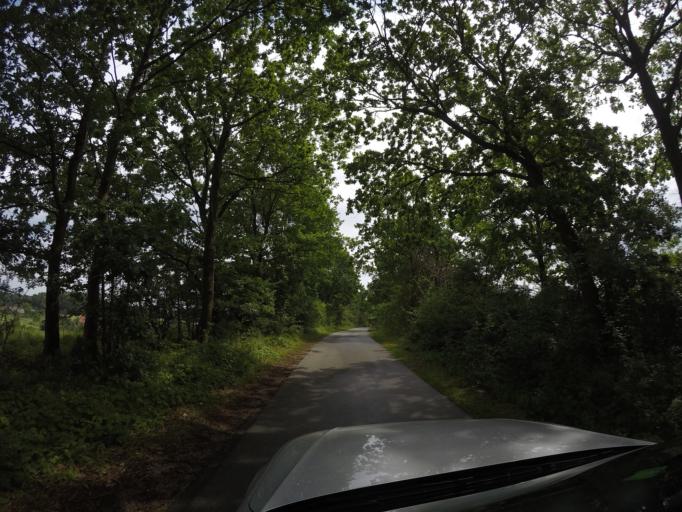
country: DE
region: Mecklenburg-Vorpommern
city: Wesenberg
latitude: 53.3623
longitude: 12.8837
